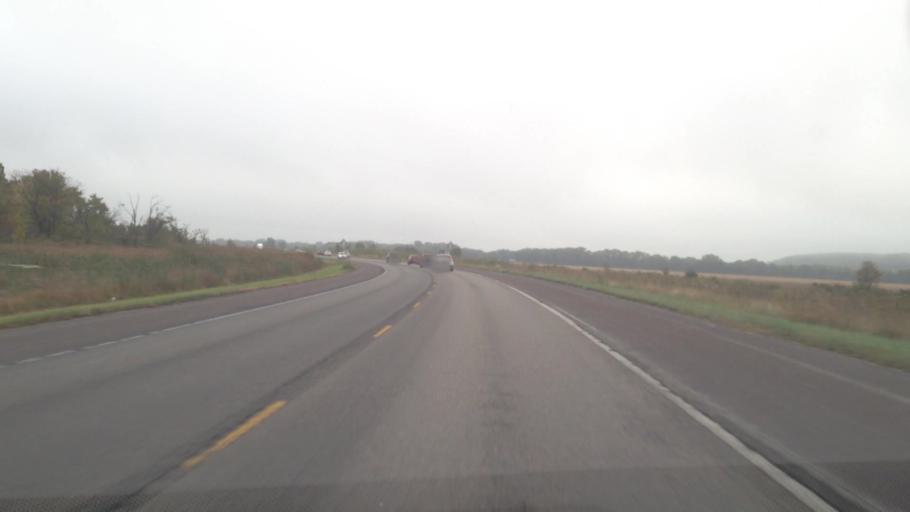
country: US
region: Kansas
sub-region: Douglas County
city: Lawrence
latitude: 38.9313
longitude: -95.3024
